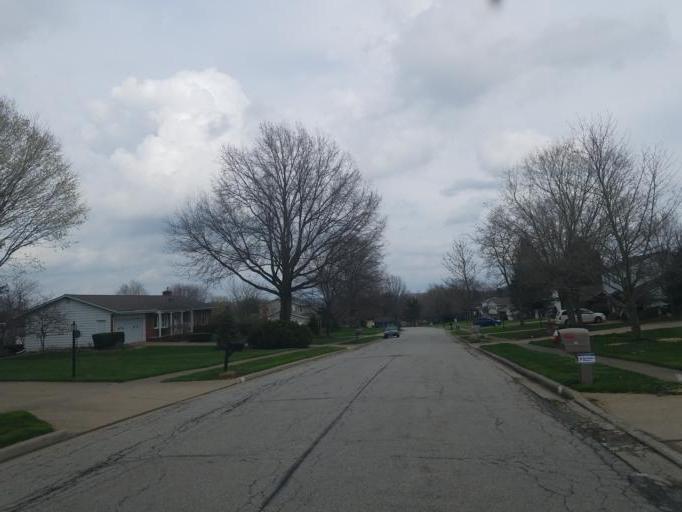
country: US
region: Ohio
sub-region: Richland County
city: Lexington
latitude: 40.6844
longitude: -82.6043
